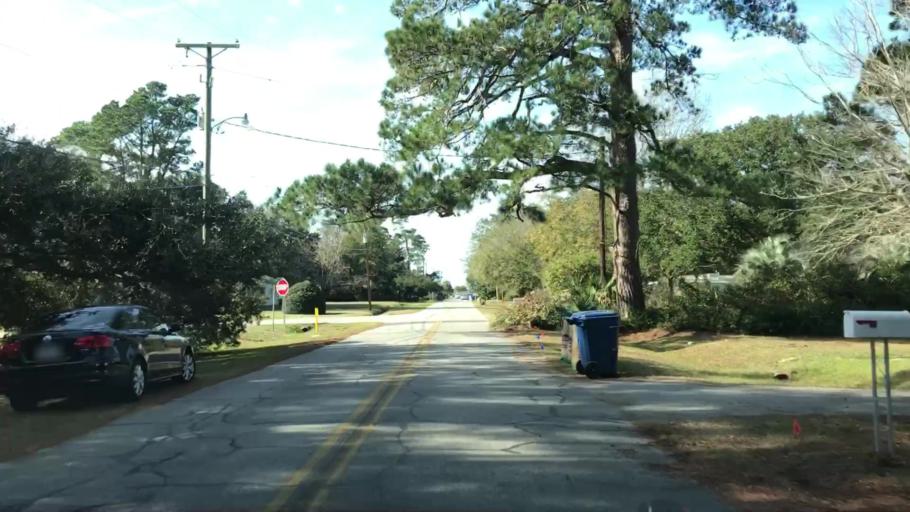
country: US
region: South Carolina
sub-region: Charleston County
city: Charleston
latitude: 32.7719
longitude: -80.0026
